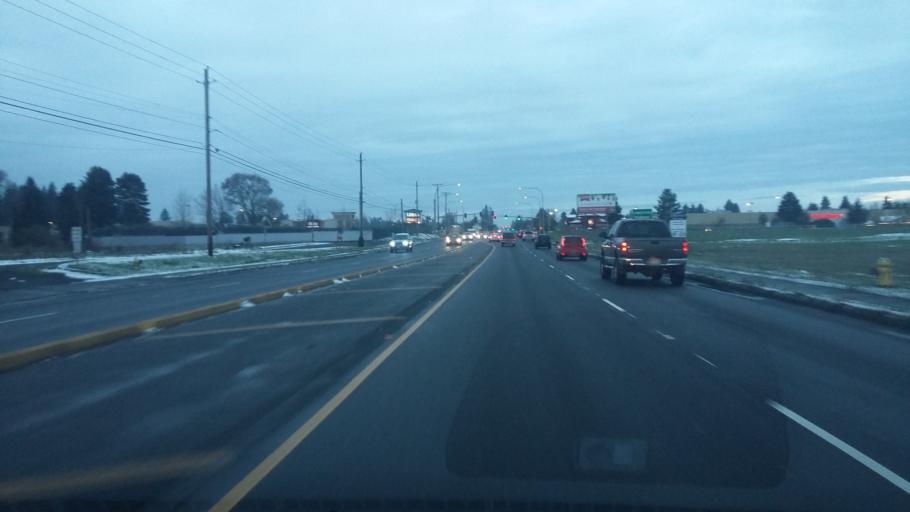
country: US
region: Washington
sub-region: Clark County
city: Orchards
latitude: 45.6724
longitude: -122.5526
